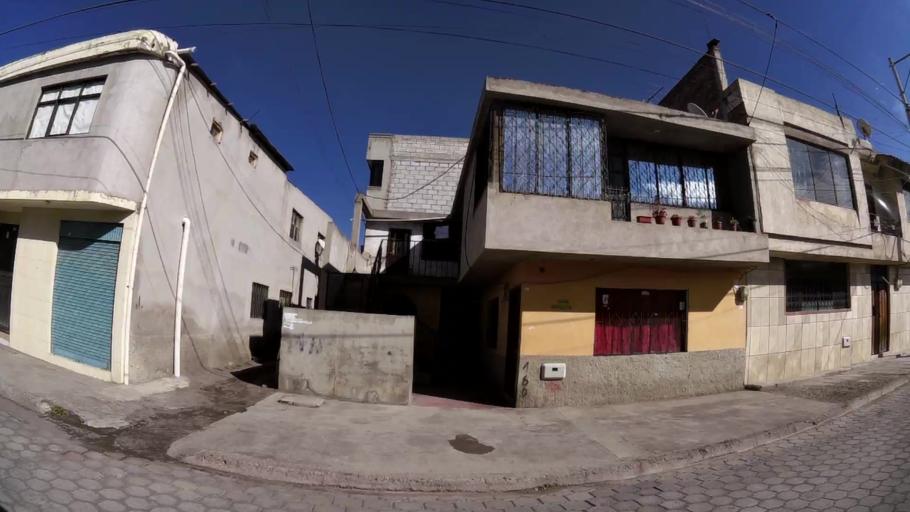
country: EC
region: Chimborazo
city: Riobamba
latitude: -1.6516
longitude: -78.6744
